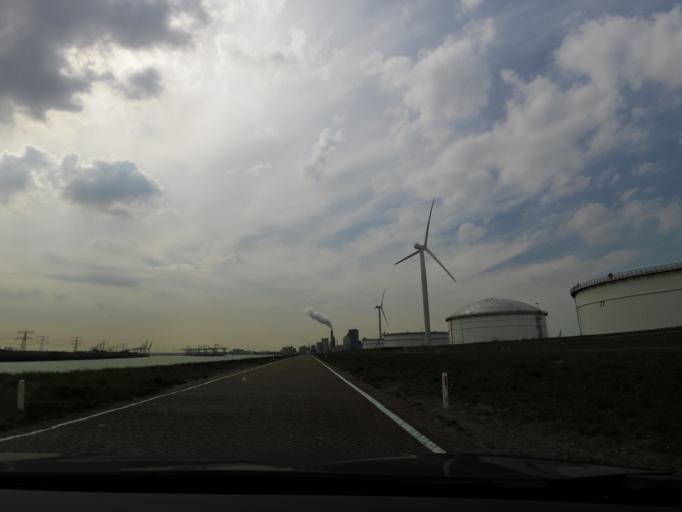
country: NL
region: South Holland
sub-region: Gemeente Rotterdam
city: Hoek van Holland
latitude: 51.9397
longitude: 4.0953
